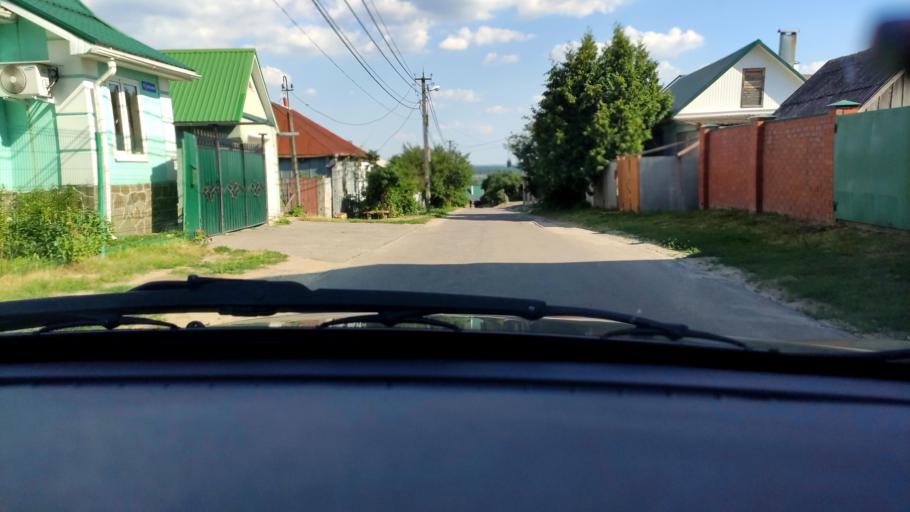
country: RU
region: Voronezj
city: Ramon'
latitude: 51.8233
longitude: 39.2742
